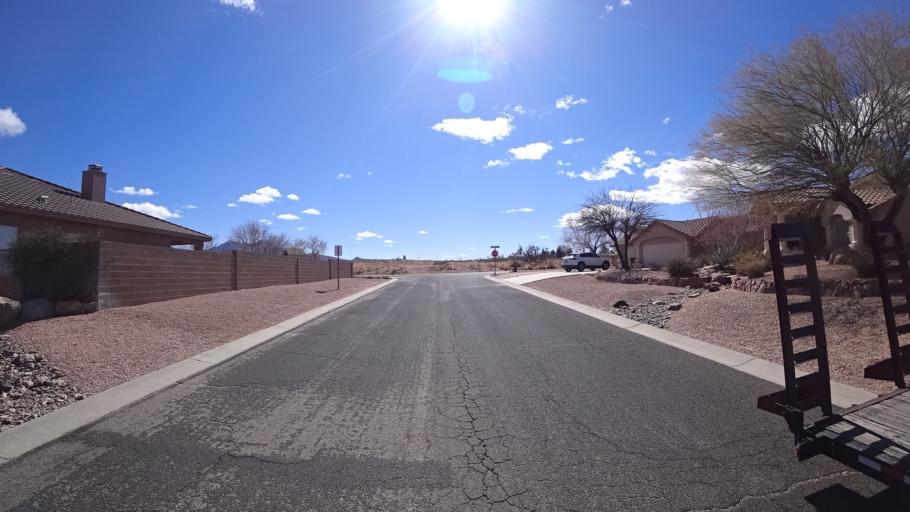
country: US
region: Arizona
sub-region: Mohave County
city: Kingman
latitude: 35.1964
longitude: -113.9754
